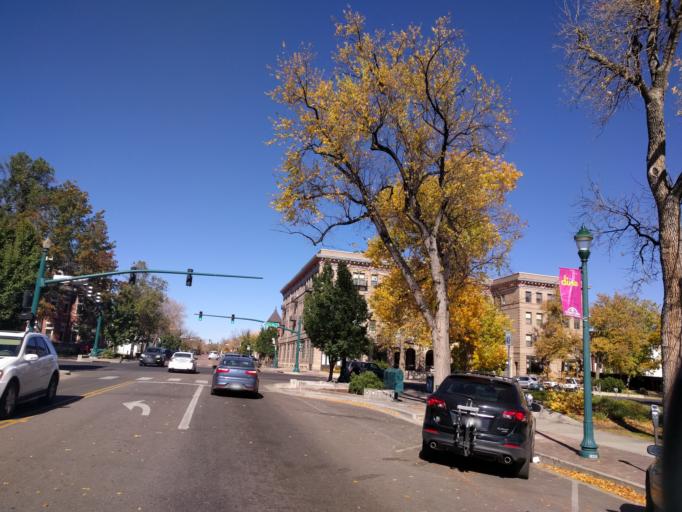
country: US
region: Colorado
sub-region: El Paso County
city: Colorado Springs
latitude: 38.8376
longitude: -104.8233
